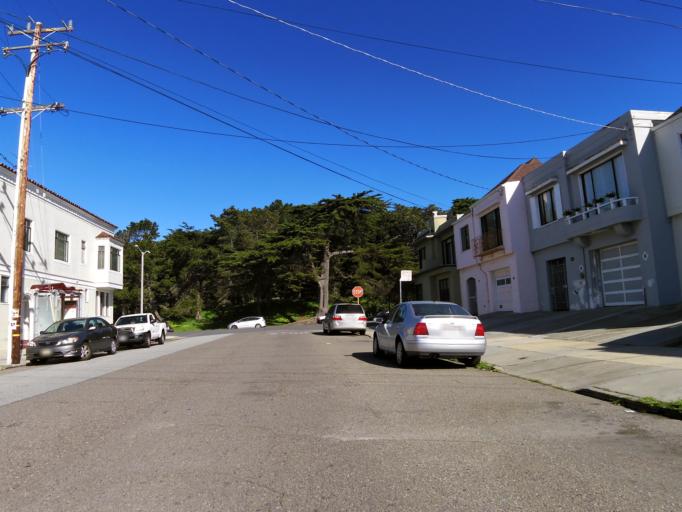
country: US
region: California
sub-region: San Mateo County
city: Daly City
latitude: 37.7637
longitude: -122.5062
